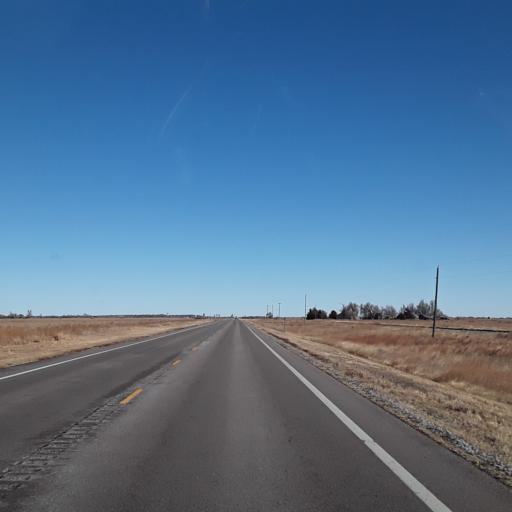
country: US
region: Kansas
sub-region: Pawnee County
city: Larned
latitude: 38.1277
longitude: -99.1681
